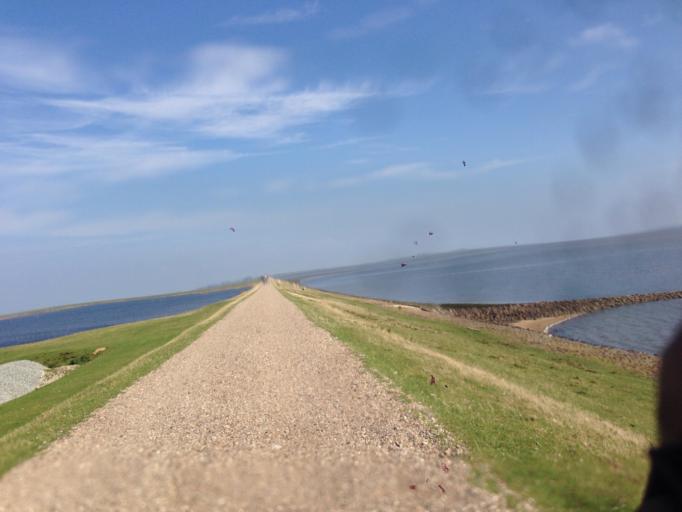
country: DE
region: Schleswig-Holstein
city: Tinnum
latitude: 54.8604
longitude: 8.3139
